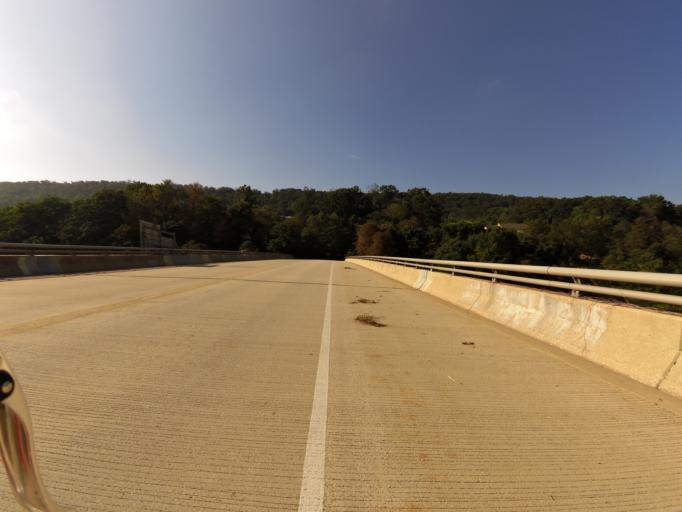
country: US
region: Pennsylvania
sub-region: Cumberland County
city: Enola
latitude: 40.3145
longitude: -76.9298
